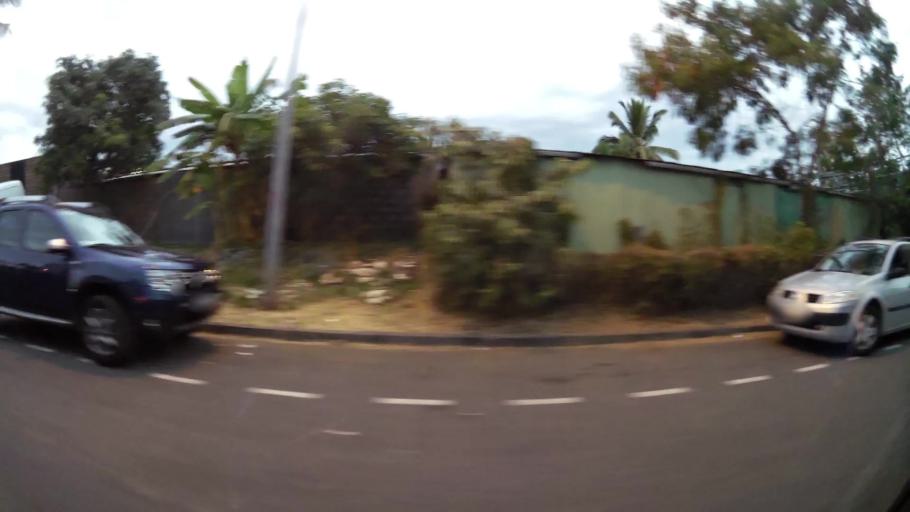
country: RE
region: Reunion
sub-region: Reunion
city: Le Port
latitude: -20.9488
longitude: 55.2950
